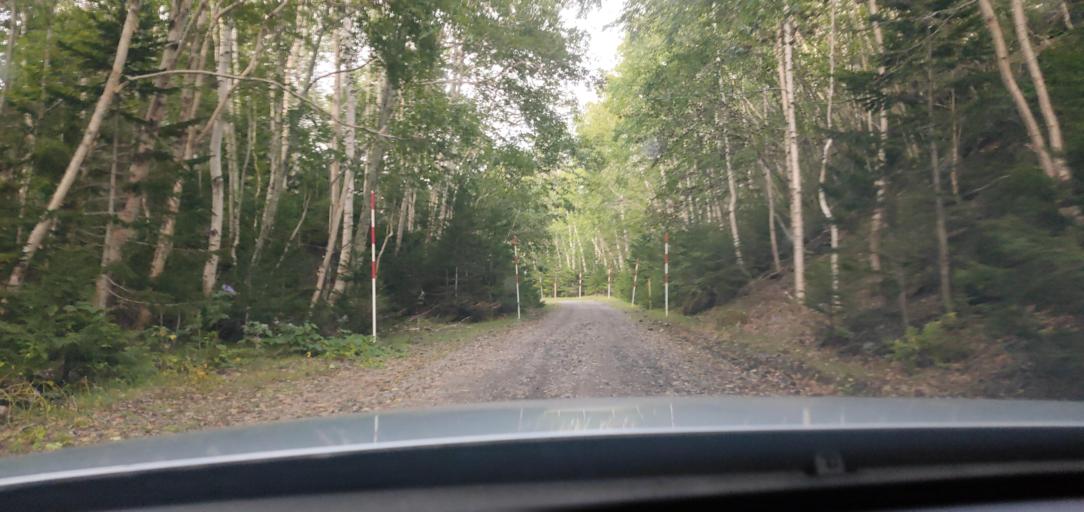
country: JP
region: Hokkaido
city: Kitami
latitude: 43.3759
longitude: 143.9680
